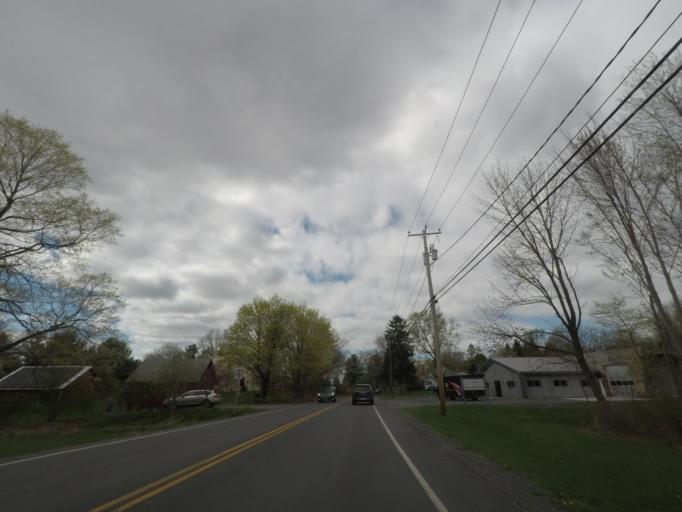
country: US
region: New York
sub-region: Columbia County
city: Chatham
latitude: 42.3613
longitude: -73.6139
